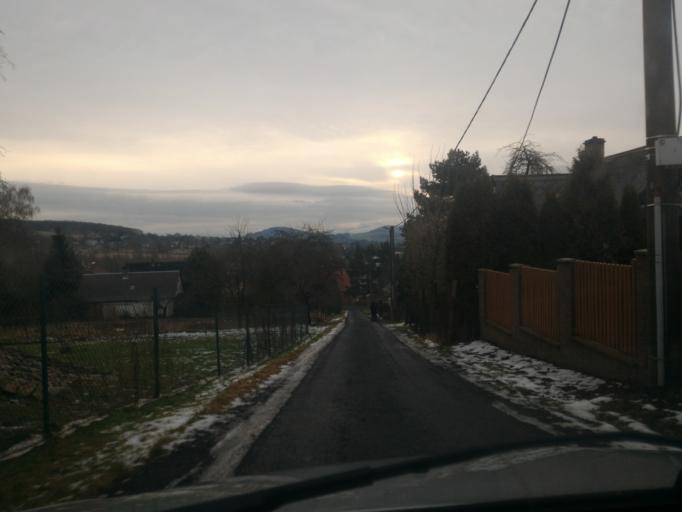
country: CZ
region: Ustecky
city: Varnsdorf
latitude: 50.9222
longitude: 14.6162
